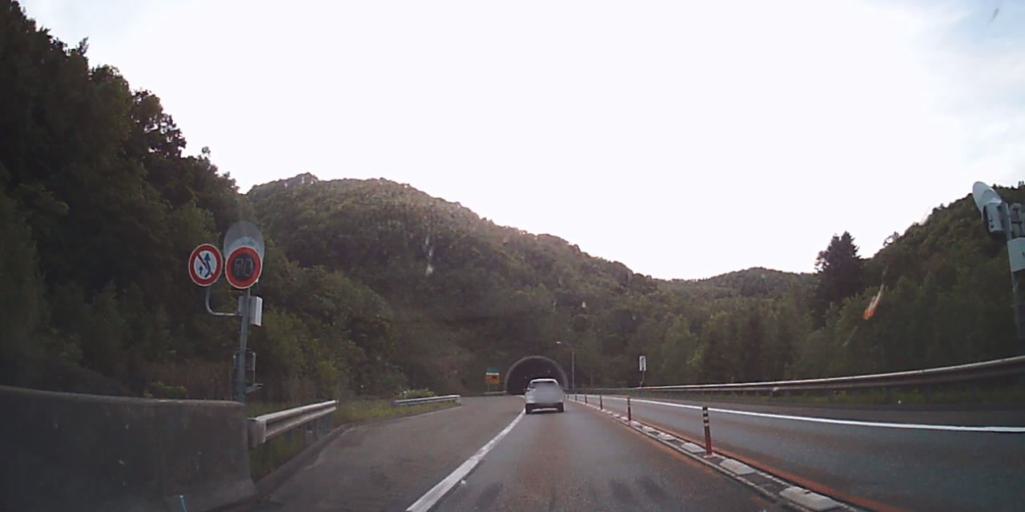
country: JP
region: Hokkaido
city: Date
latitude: 42.5729
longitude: 140.7464
